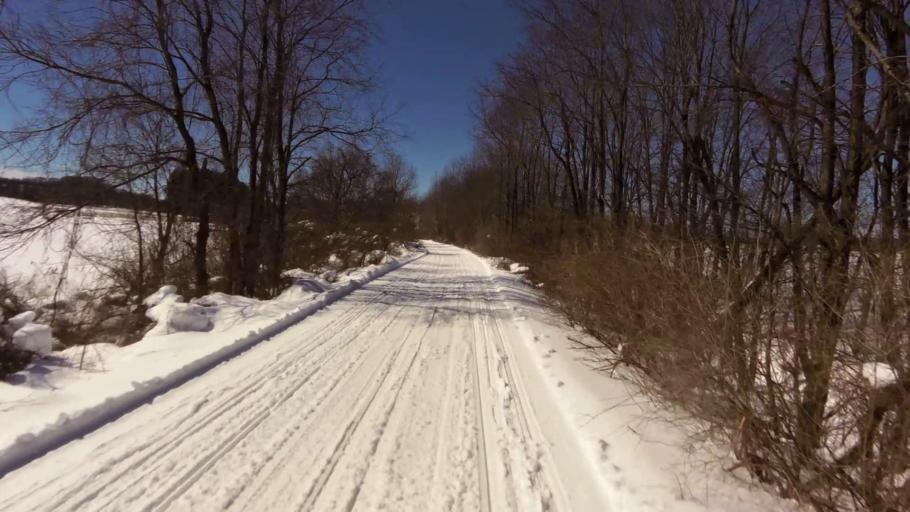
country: US
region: New York
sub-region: Cattaraugus County
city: Delevan
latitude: 42.4398
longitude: -78.4244
